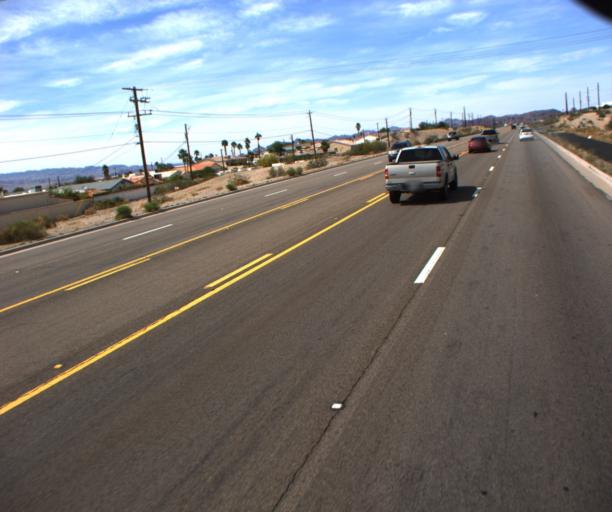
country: US
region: Arizona
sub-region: Mohave County
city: Lake Havasu City
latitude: 34.5118
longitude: -114.3494
